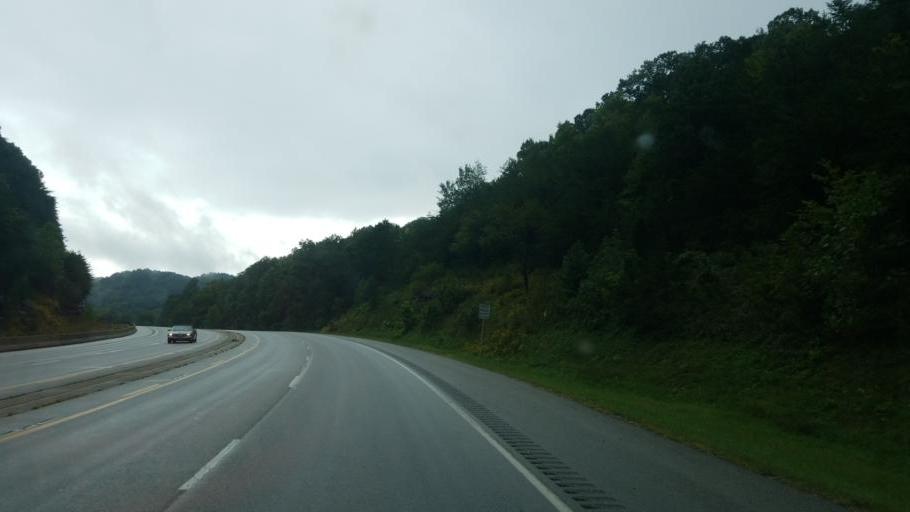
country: US
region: Kentucky
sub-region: Rowan County
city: Morehead
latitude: 38.1809
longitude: -83.4676
